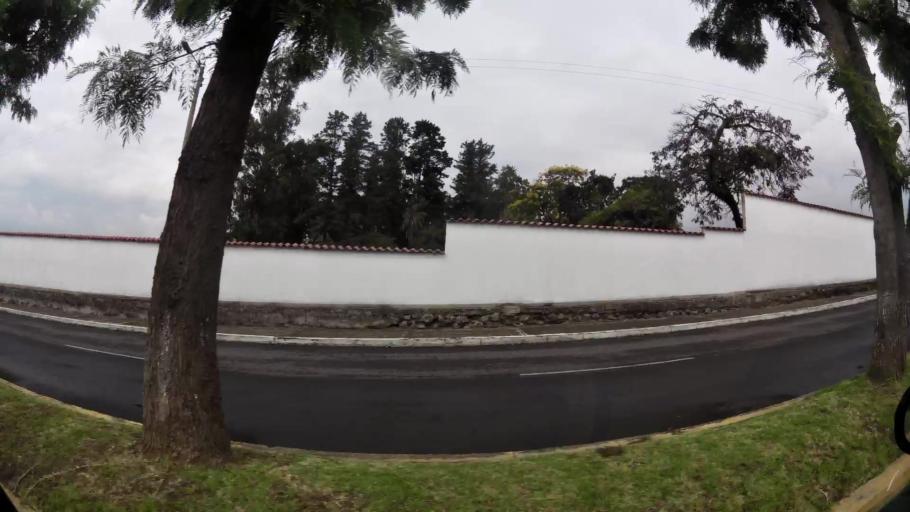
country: EC
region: Pichincha
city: Sangolqui
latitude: -0.3048
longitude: -78.4792
